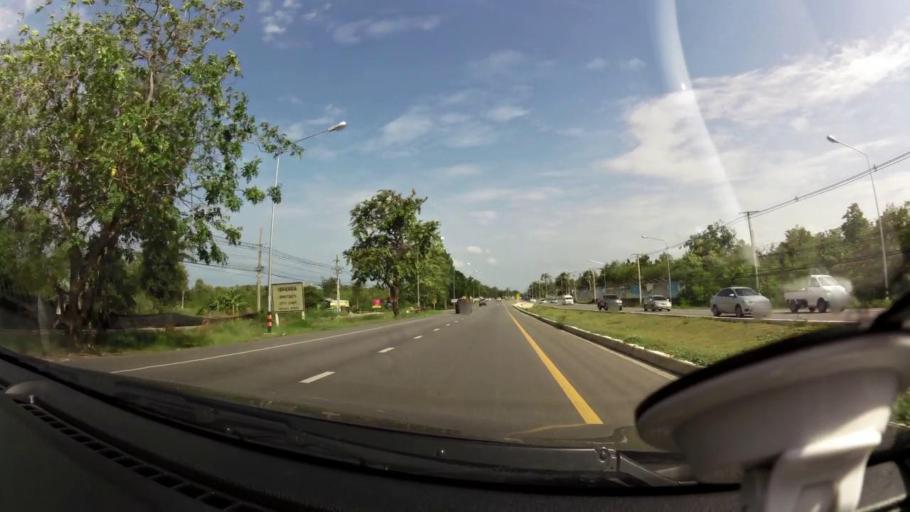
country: TH
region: Prachuap Khiri Khan
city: Hua Hin
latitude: 12.5163
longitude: 99.9654
